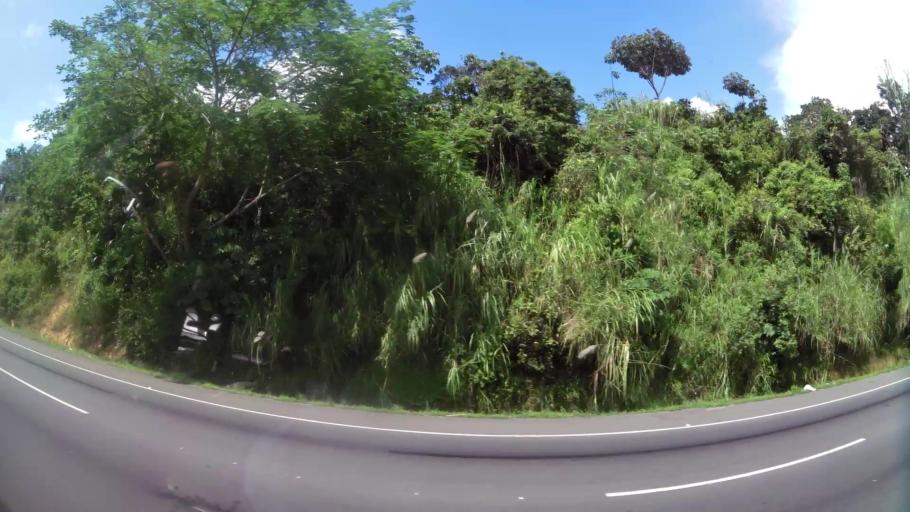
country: PA
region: Panama
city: San Vicente de Bique
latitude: 8.9342
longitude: -79.6814
